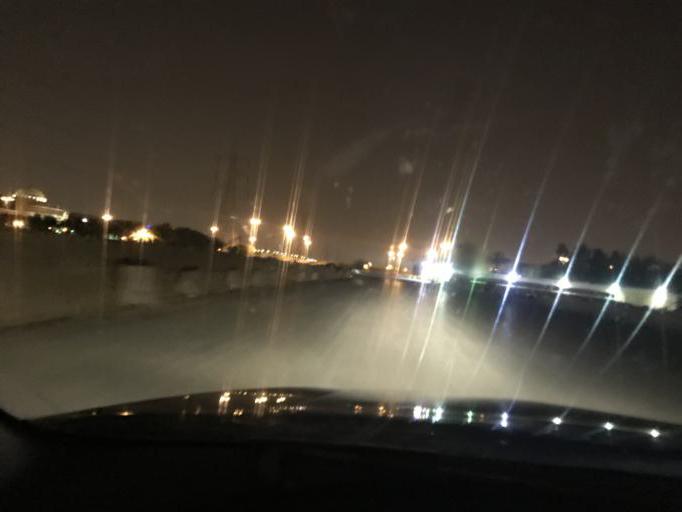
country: SA
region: Ar Riyad
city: Riyadh
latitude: 24.8114
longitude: 46.7192
